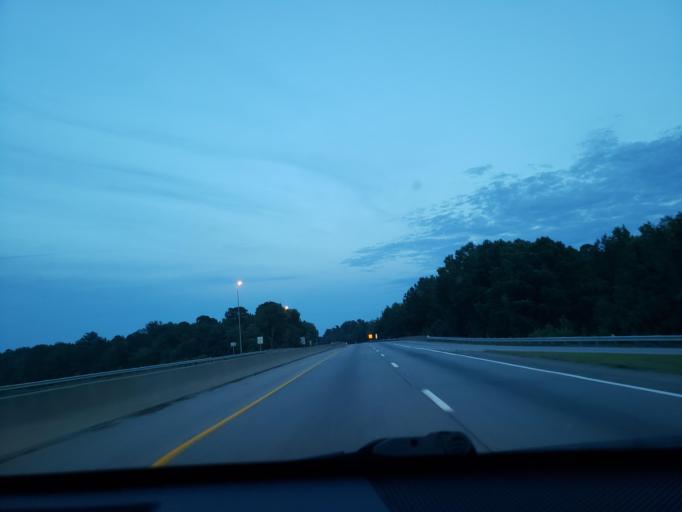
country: US
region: Virginia
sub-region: City of Franklin
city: Franklin
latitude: 36.6648
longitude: -76.9562
